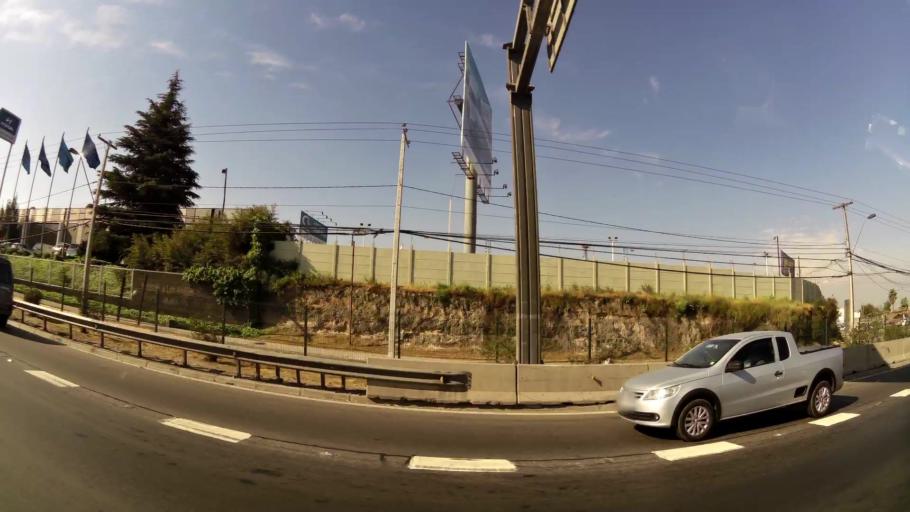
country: CL
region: Santiago Metropolitan
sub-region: Provincia de Santiago
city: Lo Prado
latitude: -33.4507
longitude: -70.7736
